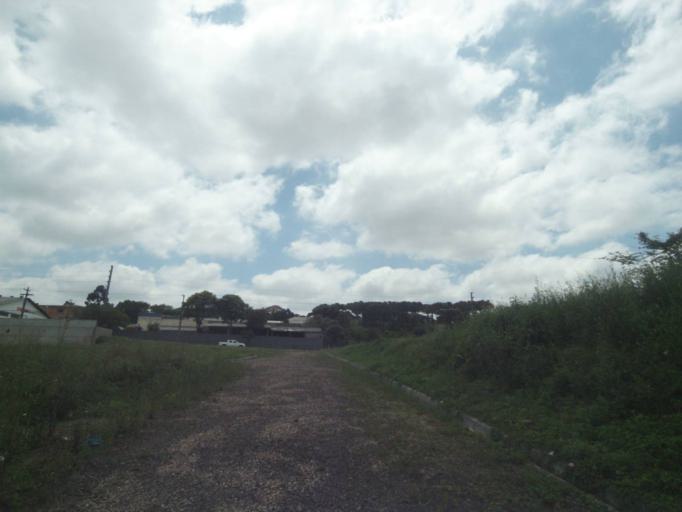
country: BR
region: Parana
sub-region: Curitiba
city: Curitiba
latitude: -25.5160
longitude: -49.3148
